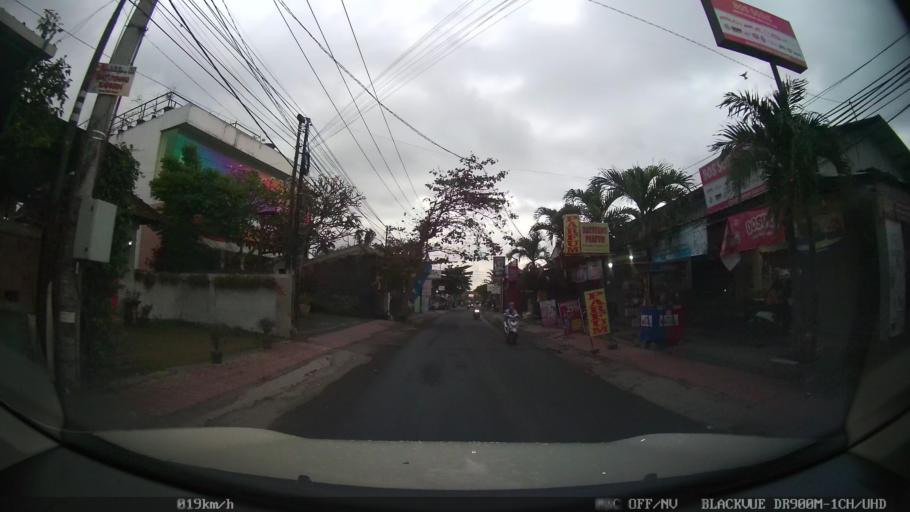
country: ID
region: Bali
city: Banjar Kertajiwa
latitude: -8.6283
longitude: 115.2610
